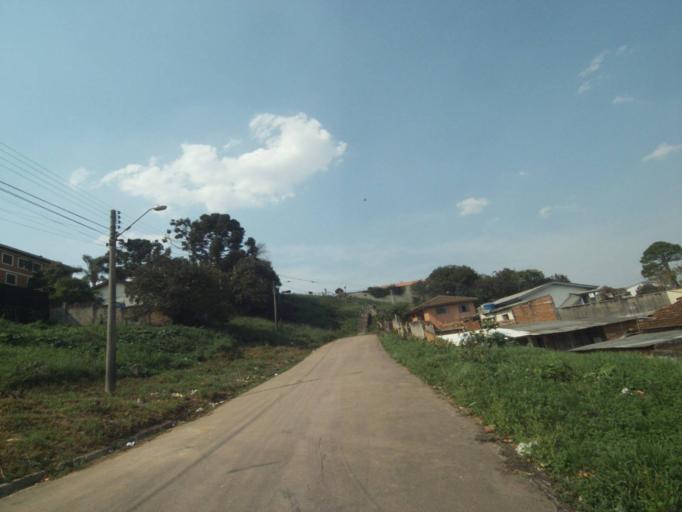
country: BR
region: Parana
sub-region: Curitiba
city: Curitiba
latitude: -25.4660
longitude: -49.2601
